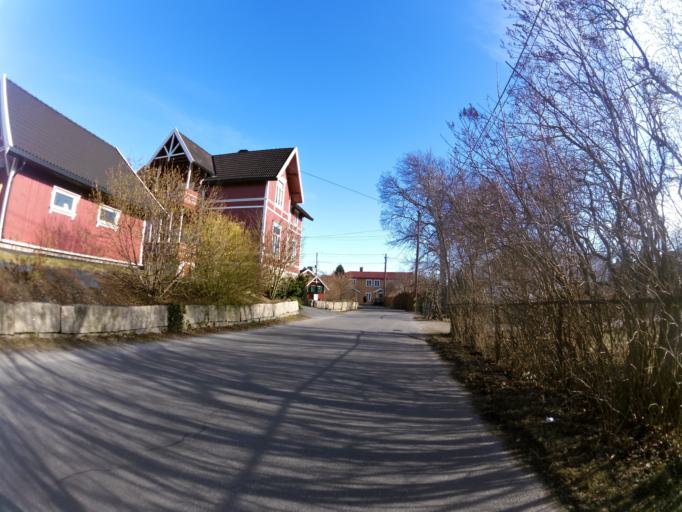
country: NO
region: Ostfold
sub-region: Fredrikstad
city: Fredrikstad
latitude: 59.2156
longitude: 10.9070
